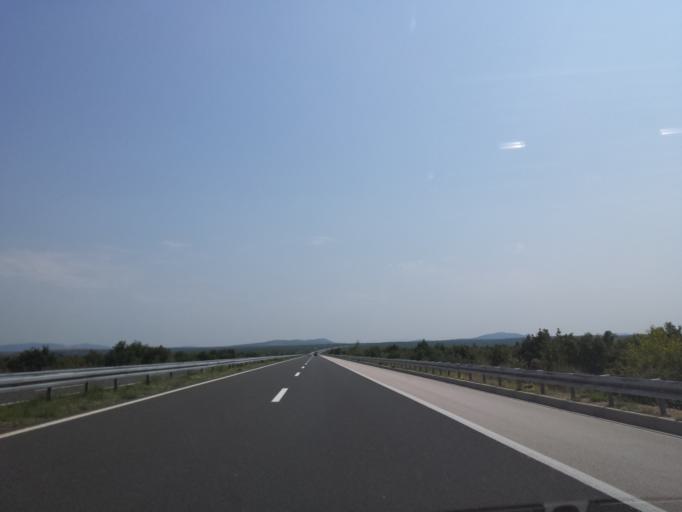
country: HR
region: Zadarska
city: Benkovac
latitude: 44.0004
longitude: 15.6042
